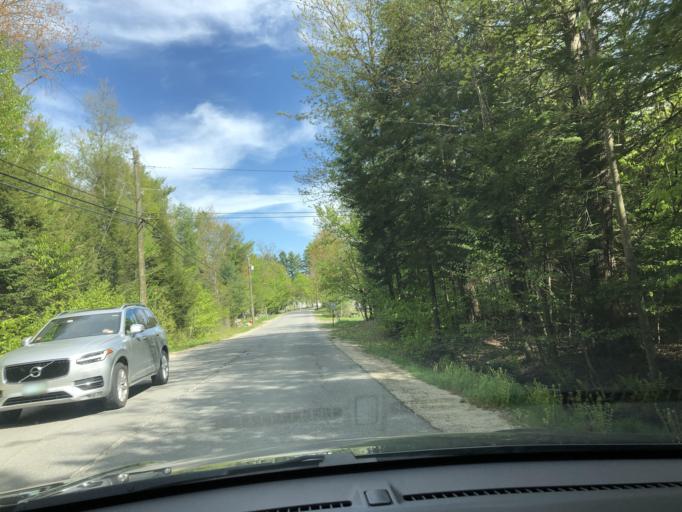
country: US
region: New Hampshire
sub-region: Merrimack County
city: New London
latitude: 43.4084
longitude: -71.9948
